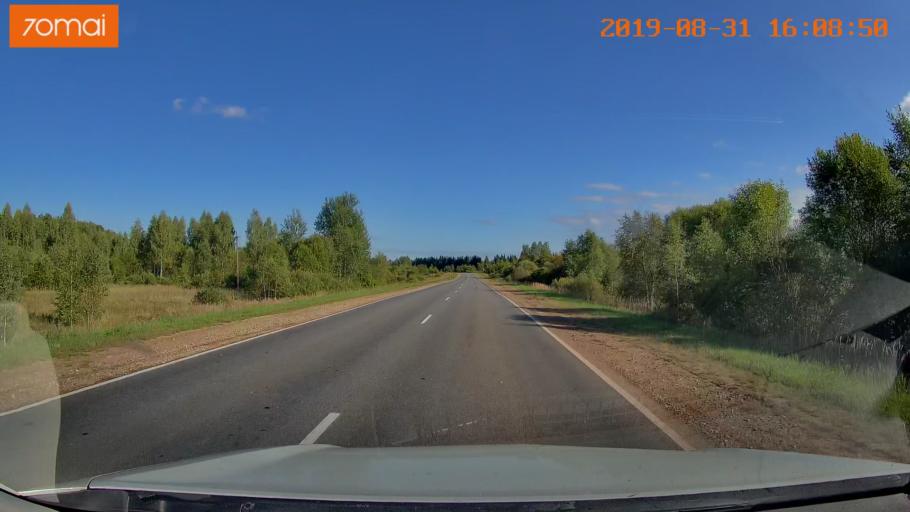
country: RU
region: Kaluga
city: Yukhnov
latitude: 54.5925
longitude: 35.3837
